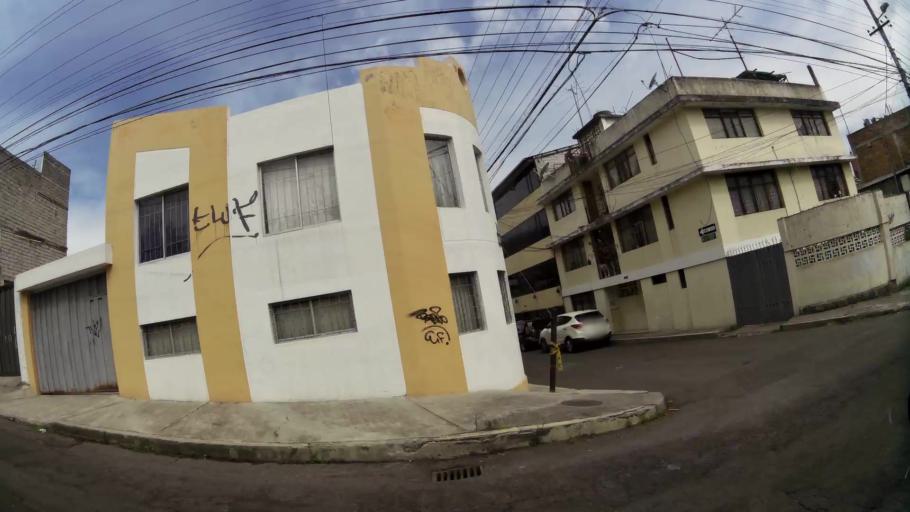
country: EC
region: Pichincha
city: Quito
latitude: -0.2141
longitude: -78.4865
